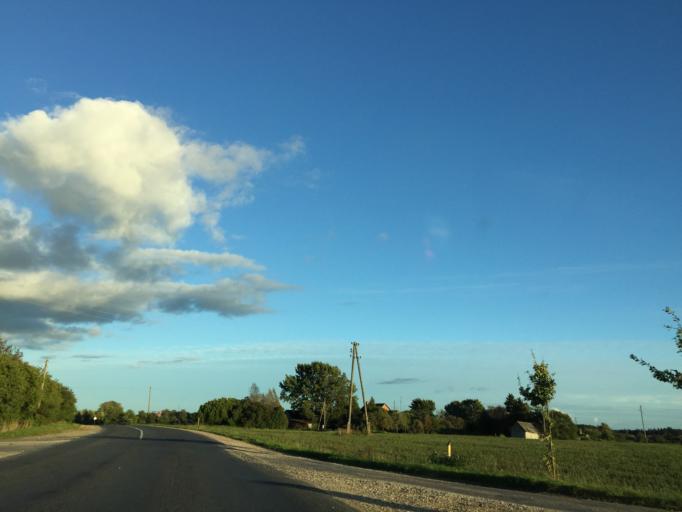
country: LV
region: Saldus Rajons
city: Saldus
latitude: 56.6959
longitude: 22.4364
